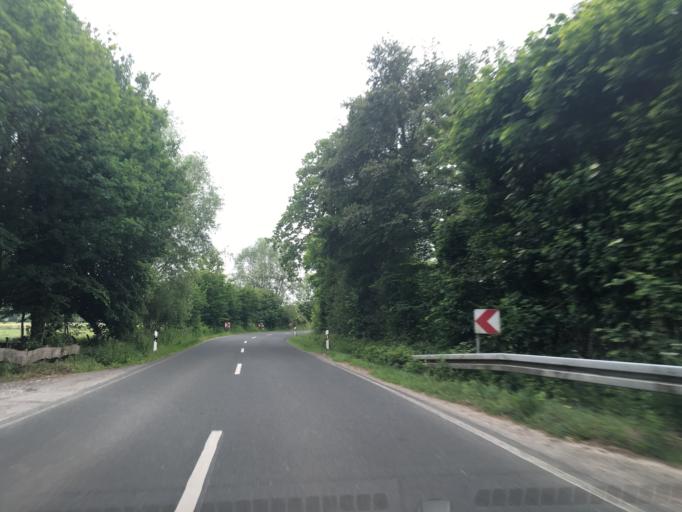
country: DE
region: North Rhine-Westphalia
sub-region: Regierungsbezirk Munster
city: Laer
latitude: 52.0870
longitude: 7.3445
